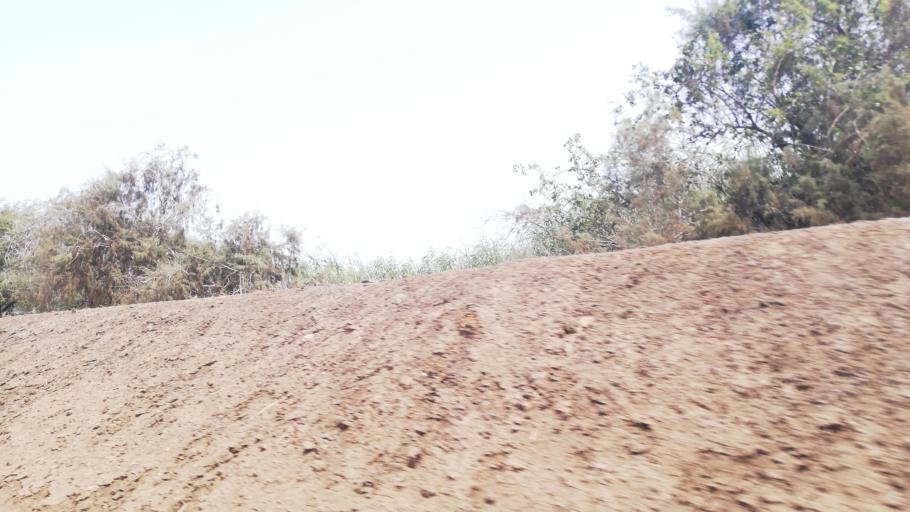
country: SN
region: Saint-Louis
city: Saint-Louis
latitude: 16.4046
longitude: -16.2952
